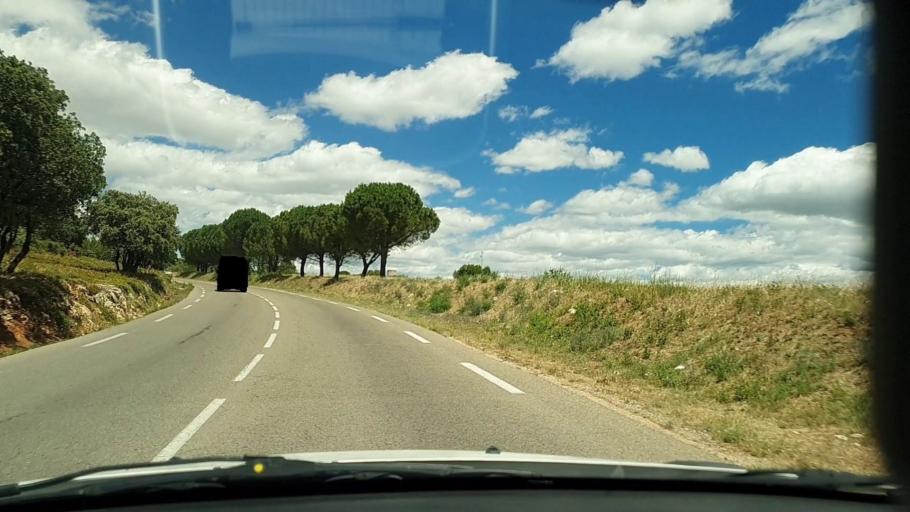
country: FR
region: Languedoc-Roussillon
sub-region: Departement du Gard
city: Poulx
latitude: 43.8971
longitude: 4.4230
